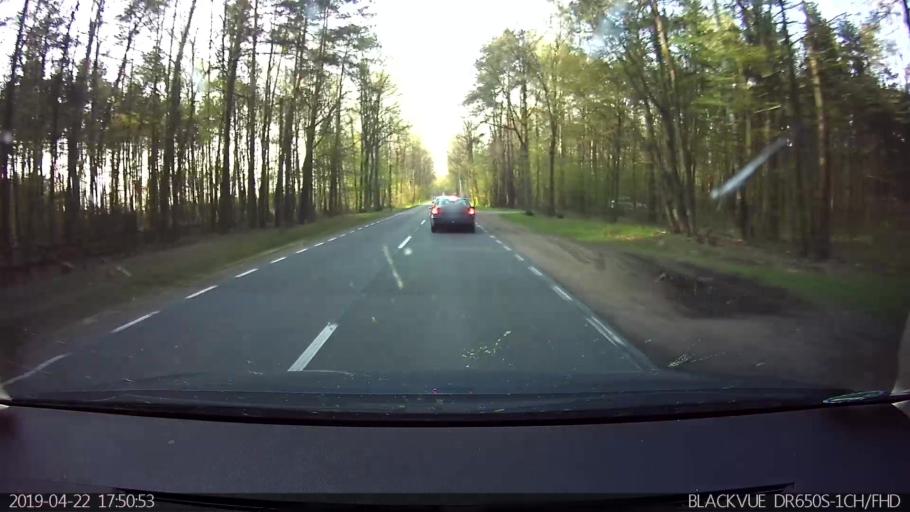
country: PL
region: Masovian Voivodeship
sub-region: Powiat wegrowski
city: Wegrow
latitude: 52.4302
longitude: 21.9982
